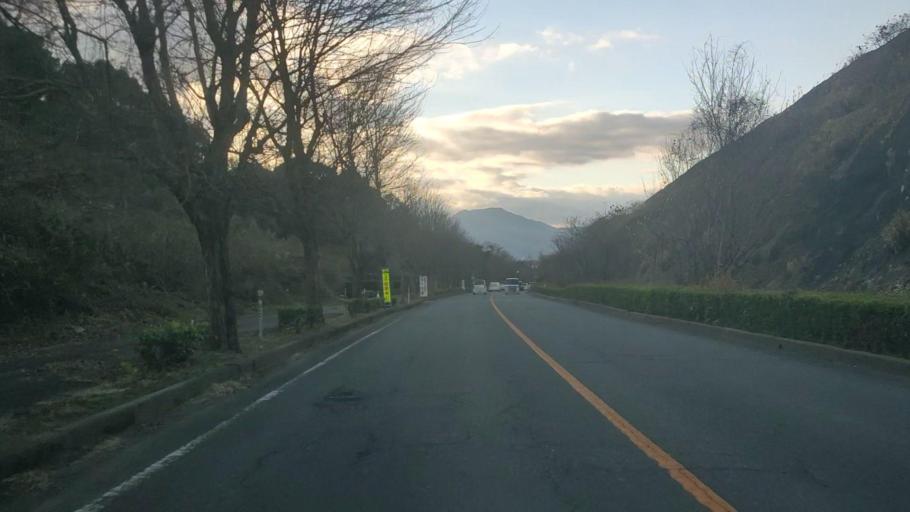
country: JP
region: Saga Prefecture
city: Saga-shi
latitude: 33.2861
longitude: 130.1543
